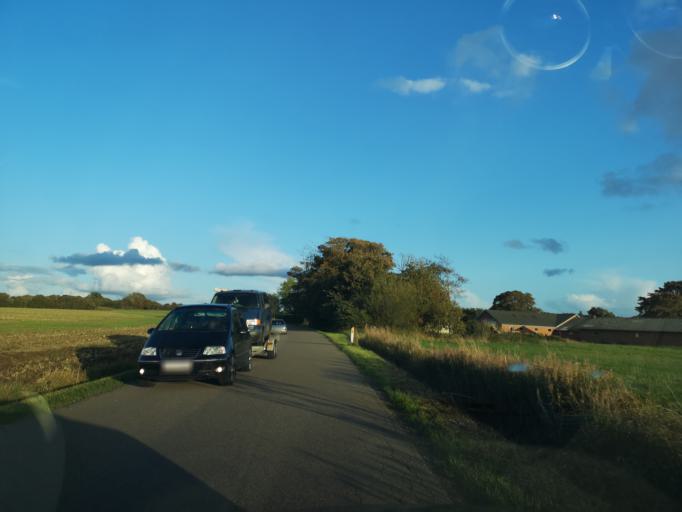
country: DK
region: Central Jutland
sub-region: Ringkobing-Skjern Kommune
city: Skjern
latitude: 55.9858
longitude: 8.5336
